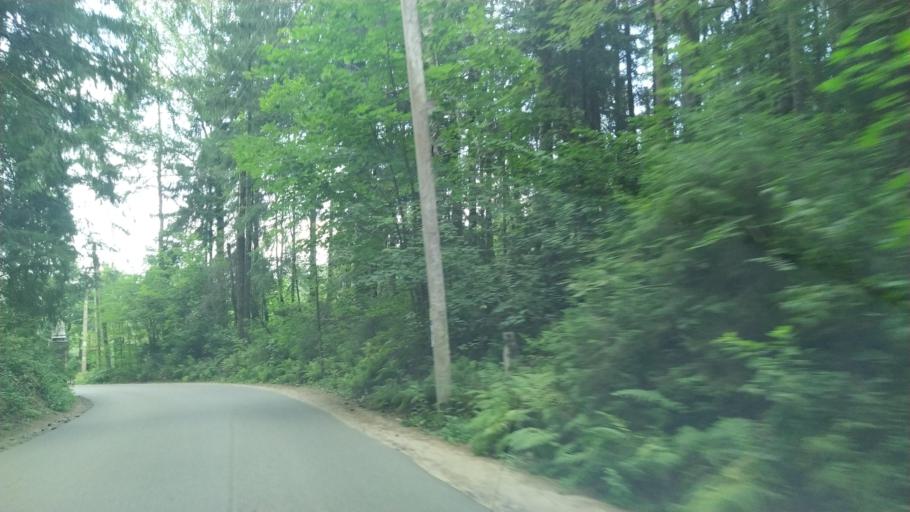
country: RU
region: Leningrad
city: Toksovo
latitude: 60.1705
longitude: 30.5324
